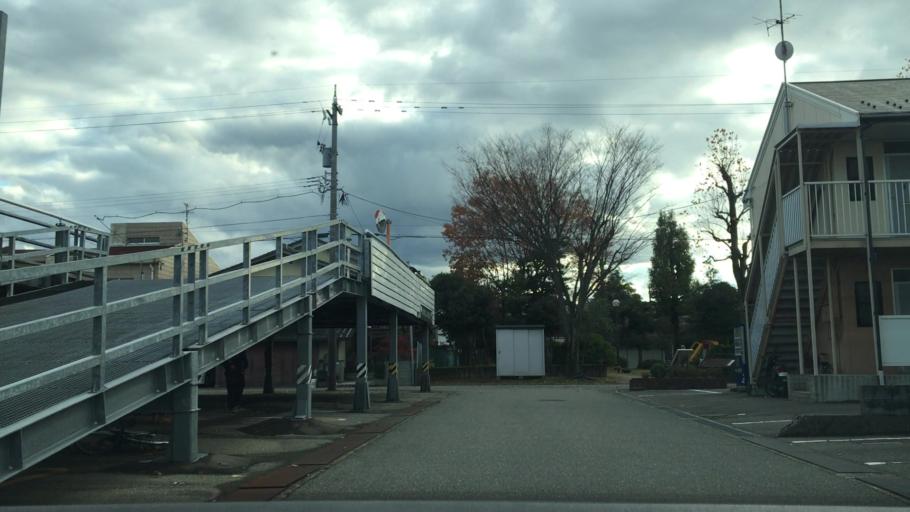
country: JP
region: Ishikawa
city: Nonoichi
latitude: 36.5216
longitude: 136.6159
